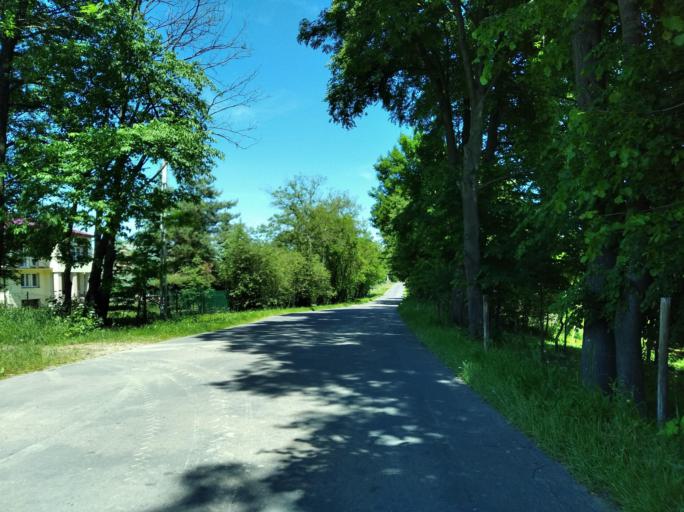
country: PL
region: Subcarpathian Voivodeship
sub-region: Powiat jasielski
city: Tarnowiec
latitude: 49.7037
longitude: 21.5526
